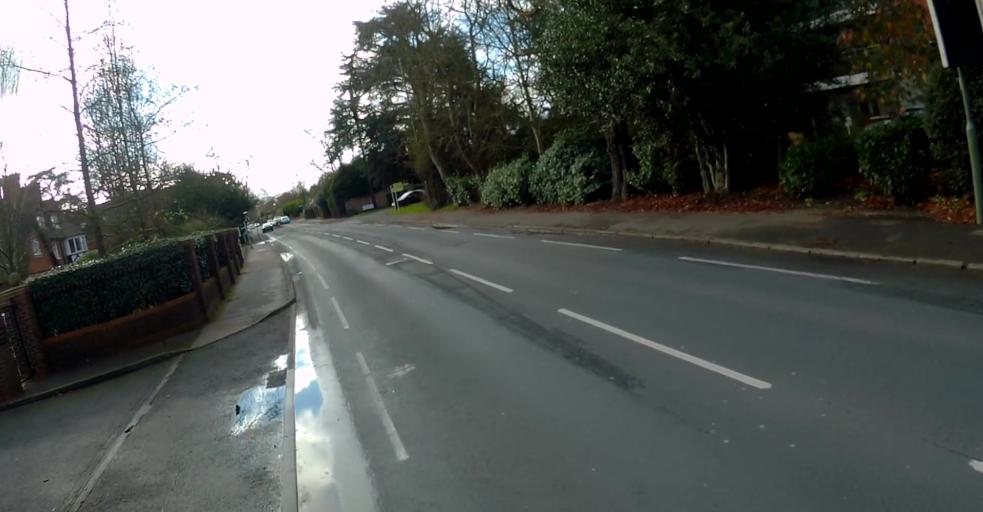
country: GB
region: England
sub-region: Surrey
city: Walton-on-Thames
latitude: 51.3787
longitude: -0.4339
